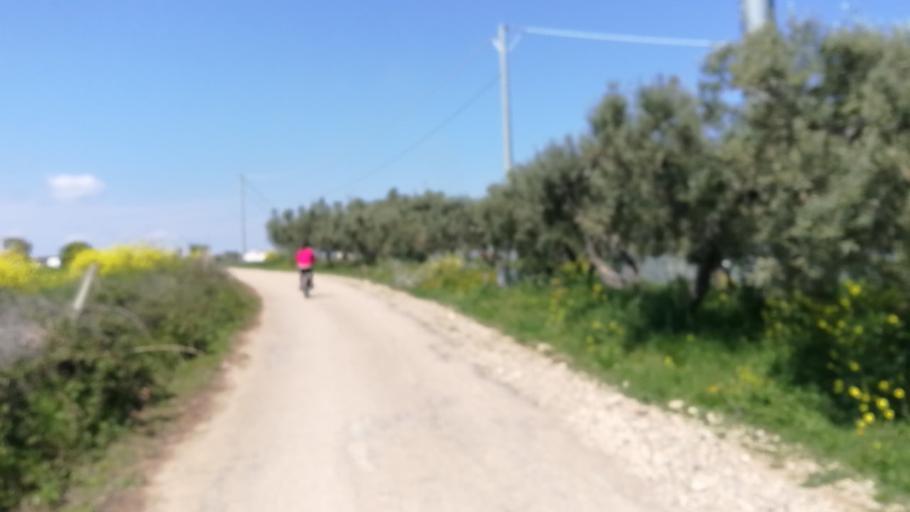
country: IT
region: Molise
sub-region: Provincia di Campobasso
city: Termoli
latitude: 41.9709
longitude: 14.9902
